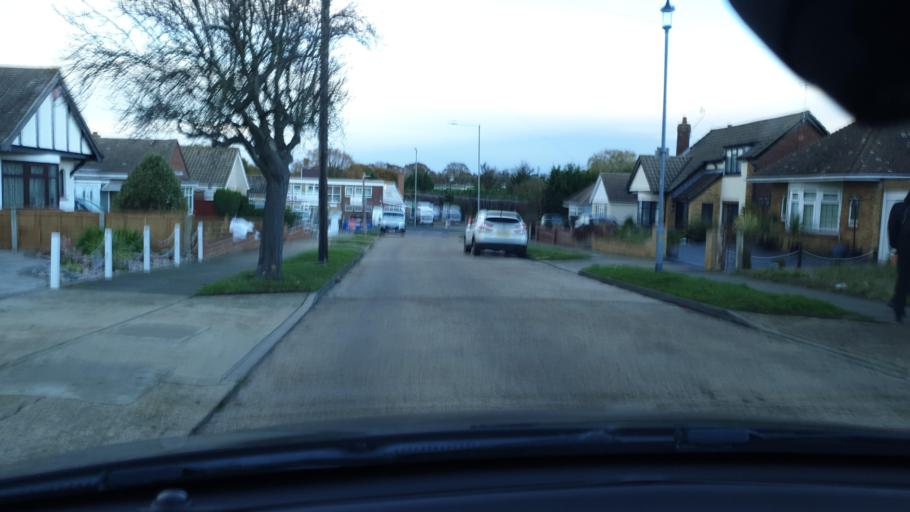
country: GB
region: England
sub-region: Essex
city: Clacton-on-Sea
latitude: 51.8022
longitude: 1.1675
